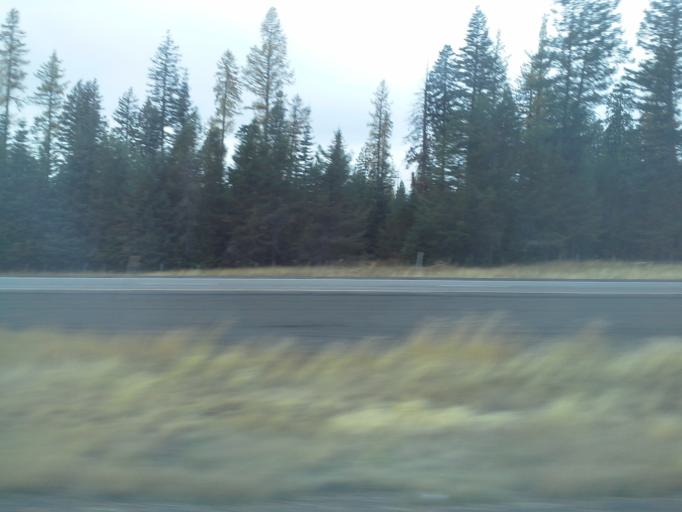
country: US
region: Oregon
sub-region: Umatilla County
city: Mission
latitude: 45.5300
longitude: -118.4473
